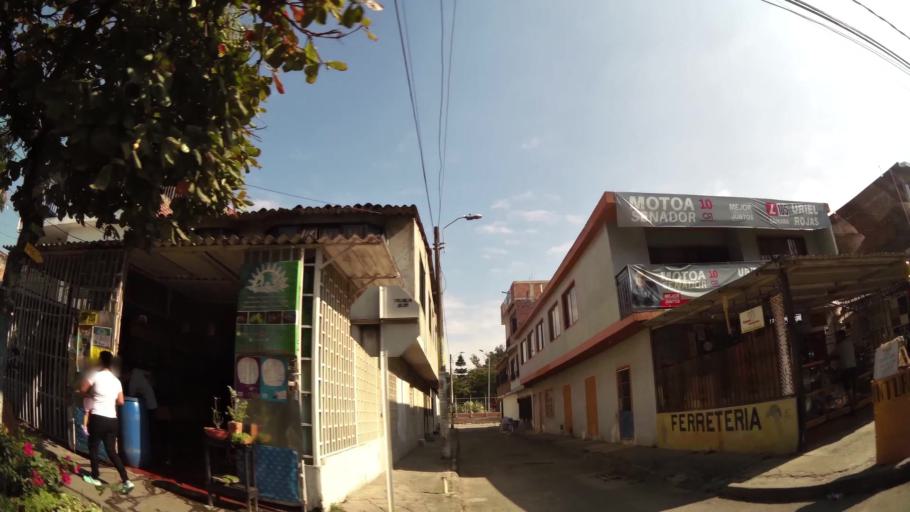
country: CO
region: Valle del Cauca
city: Cali
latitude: 3.4249
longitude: -76.5131
